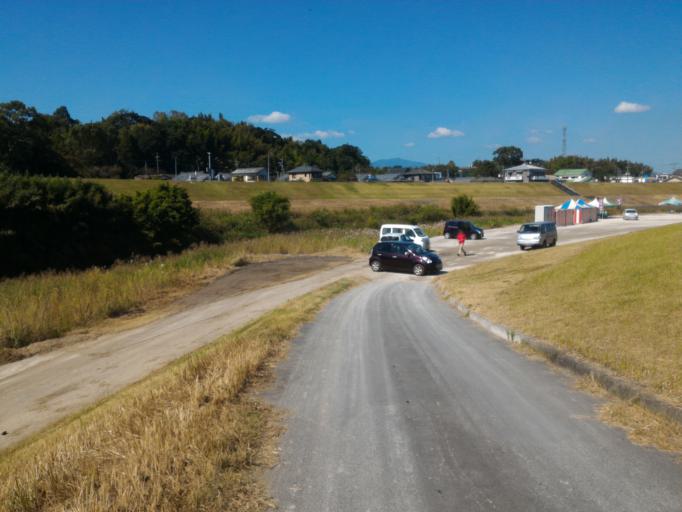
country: JP
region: Kagoshima
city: Kanoya
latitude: 31.3441
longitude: 130.9424
